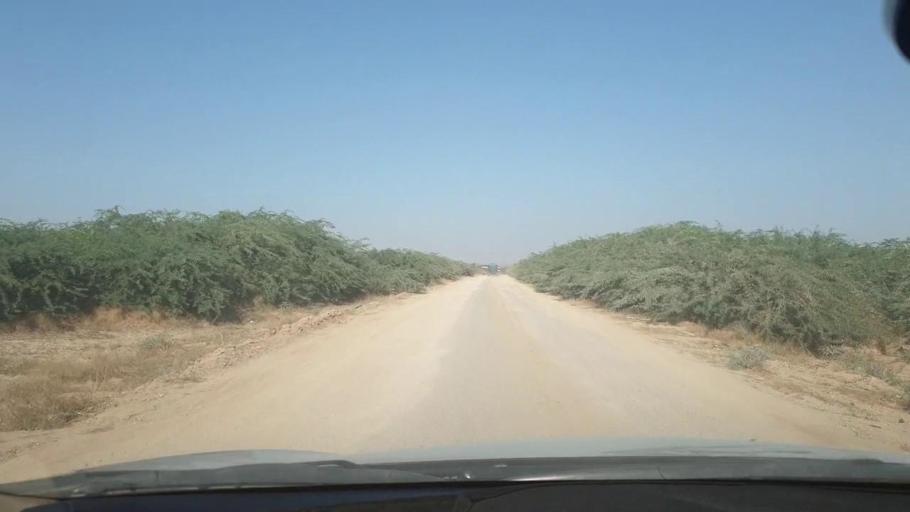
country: PK
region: Sindh
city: Malir Cantonment
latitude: 25.1427
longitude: 67.1650
